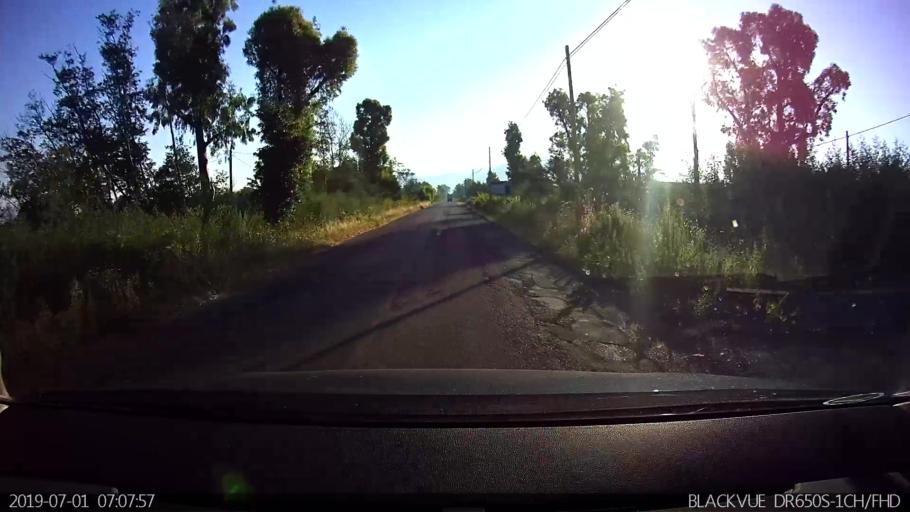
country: IT
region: Latium
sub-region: Provincia di Latina
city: Borgo Hermada
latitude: 41.2931
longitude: 13.1444
